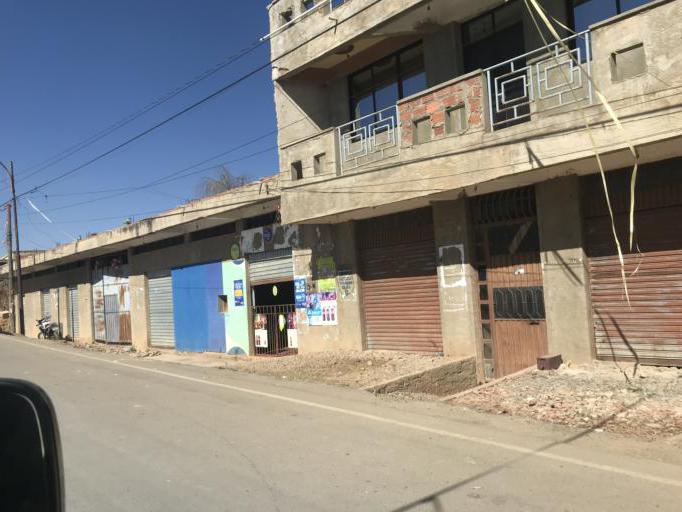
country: BO
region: Cochabamba
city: Cliza
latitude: -17.5878
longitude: -65.9228
